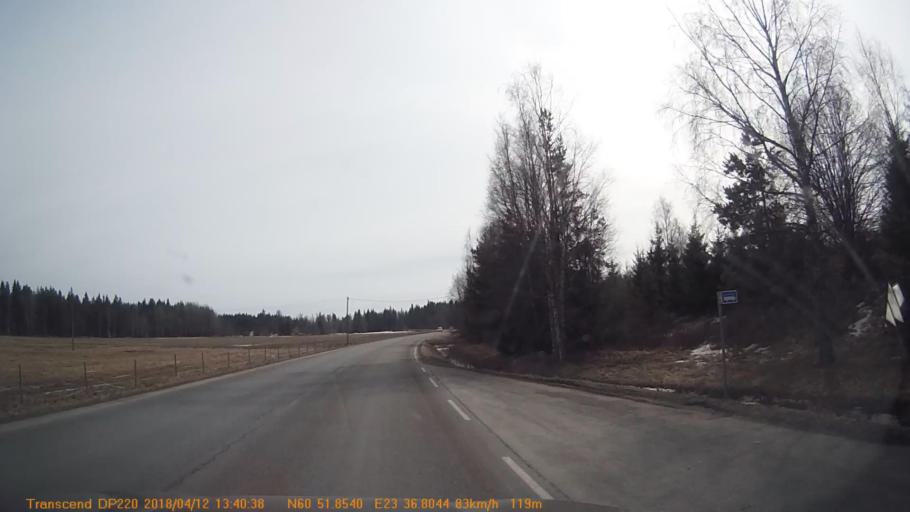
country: FI
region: Haeme
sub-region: Forssa
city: Forssa
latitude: 60.8636
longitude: 23.6137
